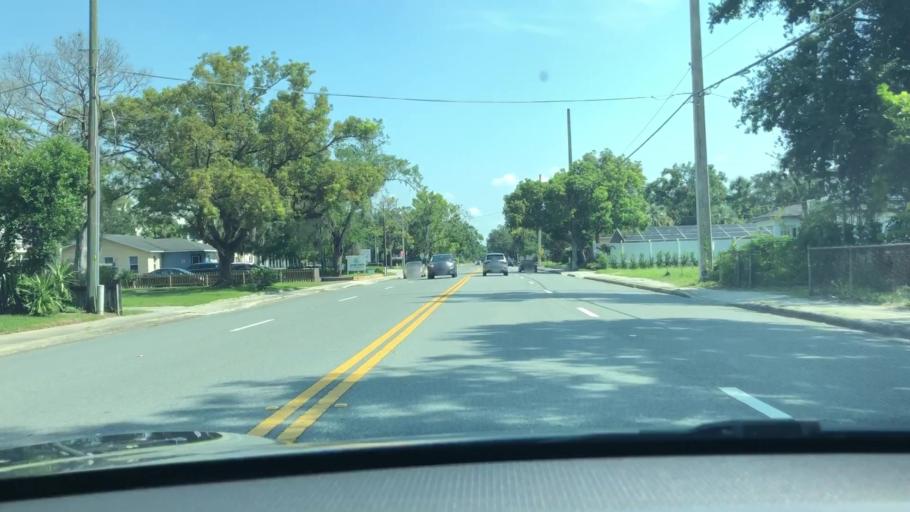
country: US
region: Florida
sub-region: Orange County
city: Winter Park
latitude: 28.6056
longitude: -81.3281
